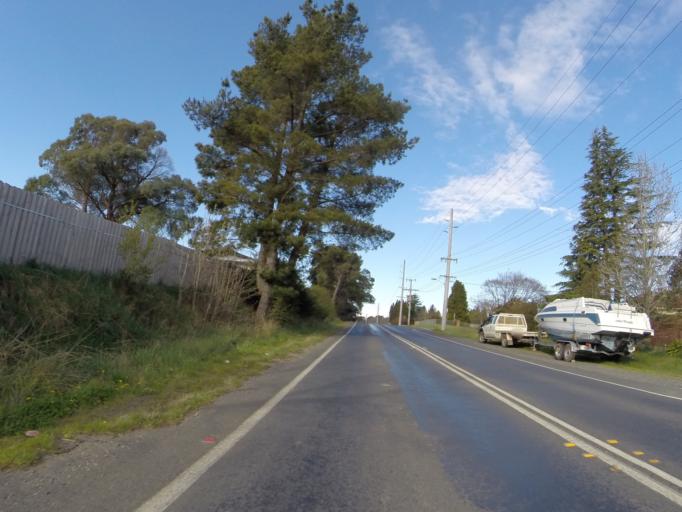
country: AU
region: New South Wales
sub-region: Wingecarribee
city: Moss Vale
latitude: -34.5551
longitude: 150.3562
